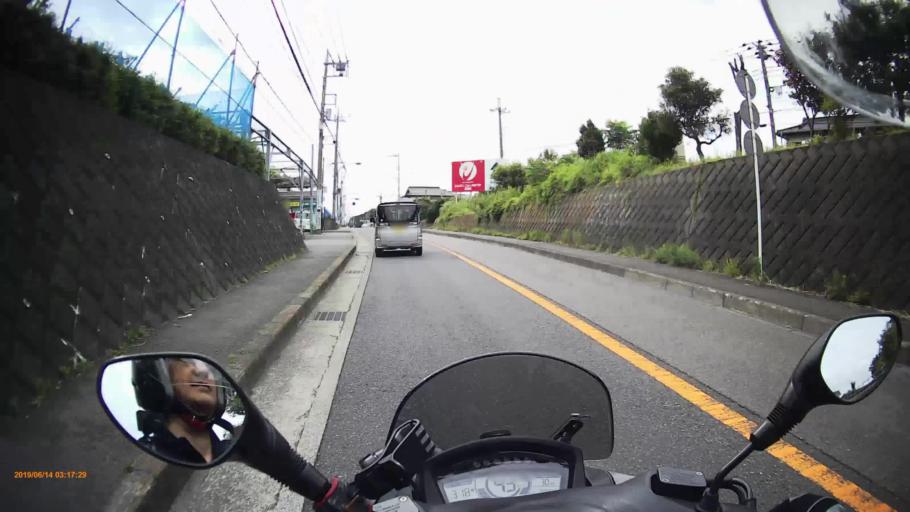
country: JP
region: Kanagawa
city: Minami-rinkan
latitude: 35.4172
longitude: 139.4590
